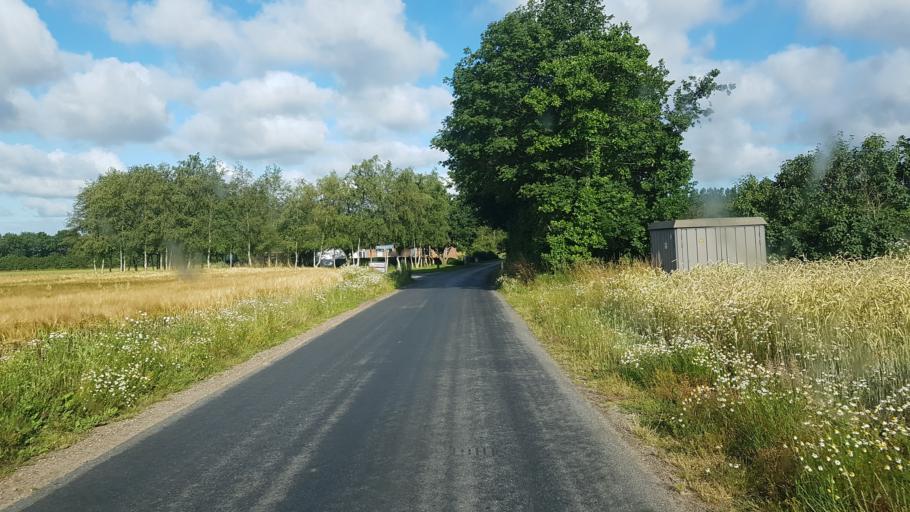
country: DK
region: South Denmark
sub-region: Vejen Kommune
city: Holsted
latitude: 55.4487
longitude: 8.8692
